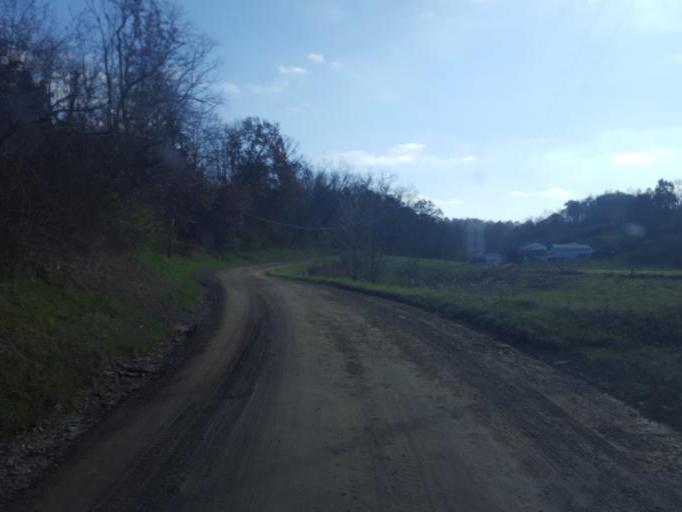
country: US
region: Ohio
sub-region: Knox County
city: Oak Hill
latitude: 40.4114
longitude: -82.2215
